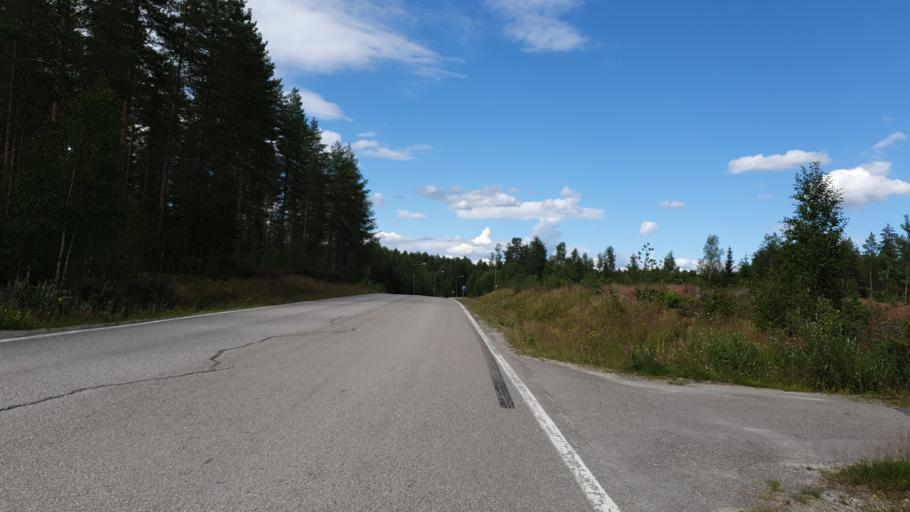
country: FI
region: Kainuu
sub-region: Kehys-Kainuu
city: Kuhmo
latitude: 64.1148
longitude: 29.5276
